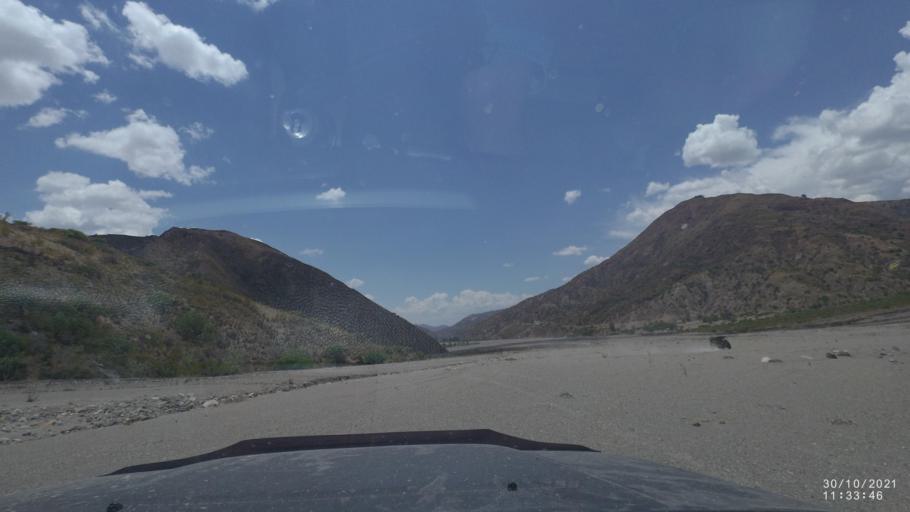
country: BO
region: Cochabamba
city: Sipe Sipe
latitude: -17.5226
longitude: -66.5926
